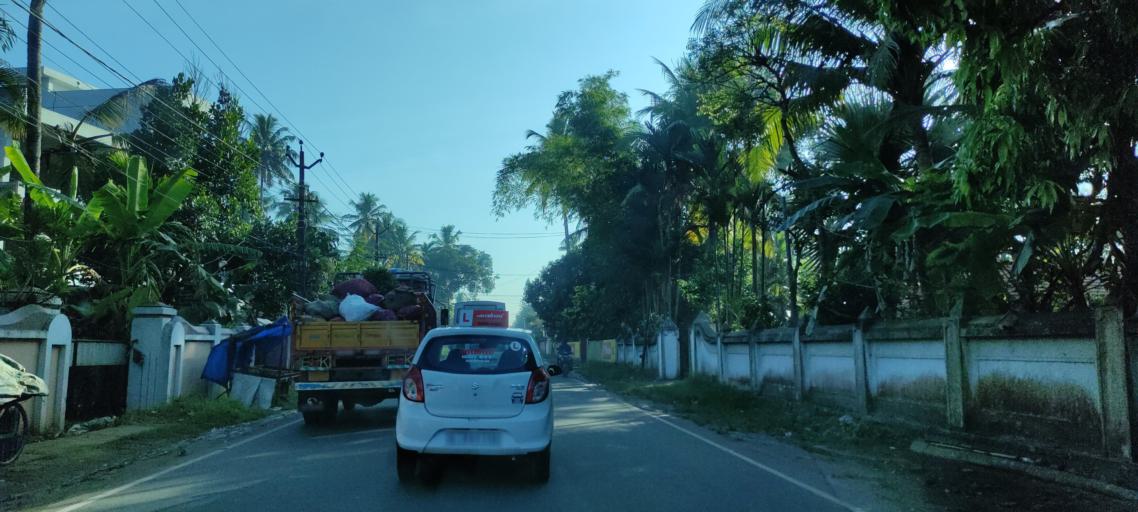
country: IN
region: Kerala
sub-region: Alappuzha
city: Kayankulam
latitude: 9.1758
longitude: 76.5143
